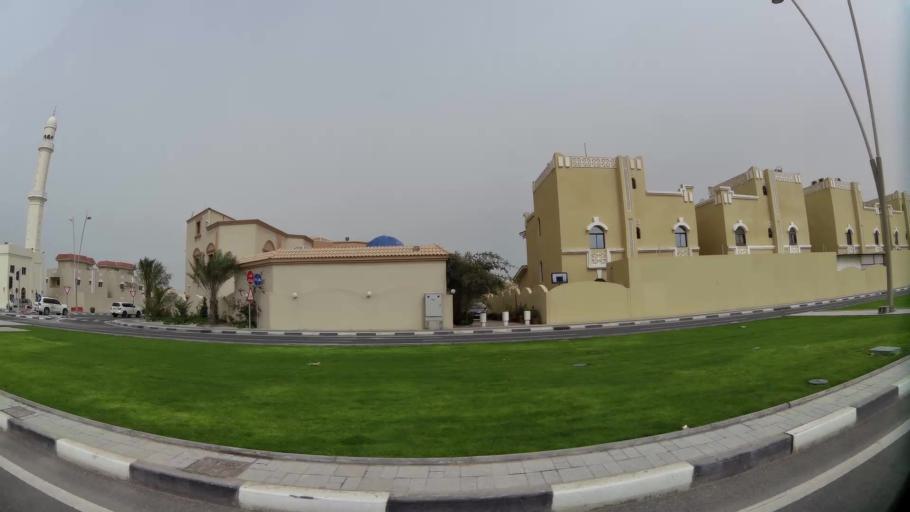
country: QA
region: Baladiyat ad Dawhah
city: Doha
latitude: 25.2294
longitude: 51.5353
